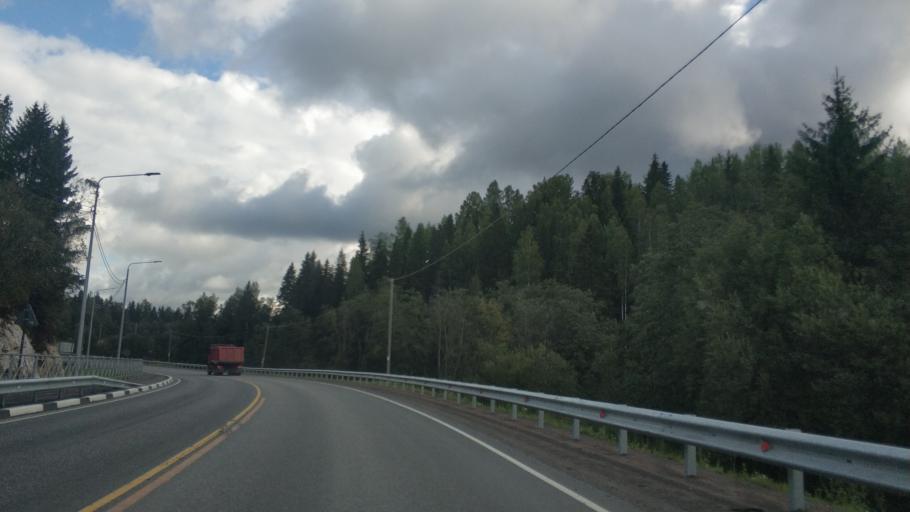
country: RU
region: Republic of Karelia
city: Ruskeala
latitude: 61.9384
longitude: 30.5915
